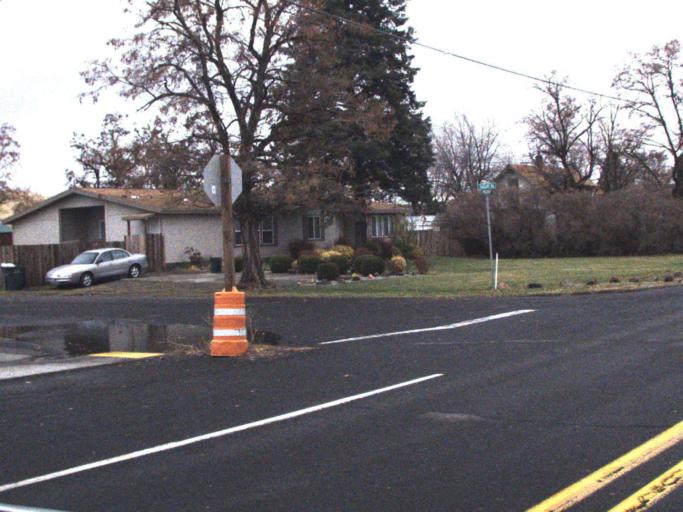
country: US
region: Washington
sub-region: Walla Walla County
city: Waitsburg
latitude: 46.2701
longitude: -118.1409
